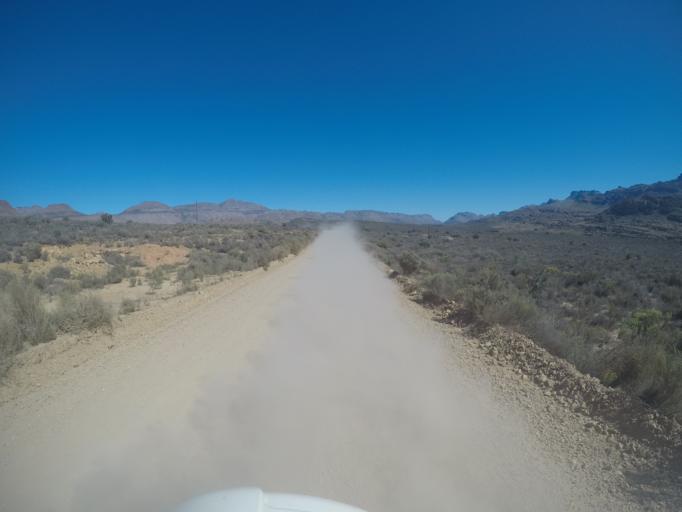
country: ZA
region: Western Cape
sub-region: West Coast District Municipality
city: Clanwilliam
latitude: -32.4955
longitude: 19.2704
